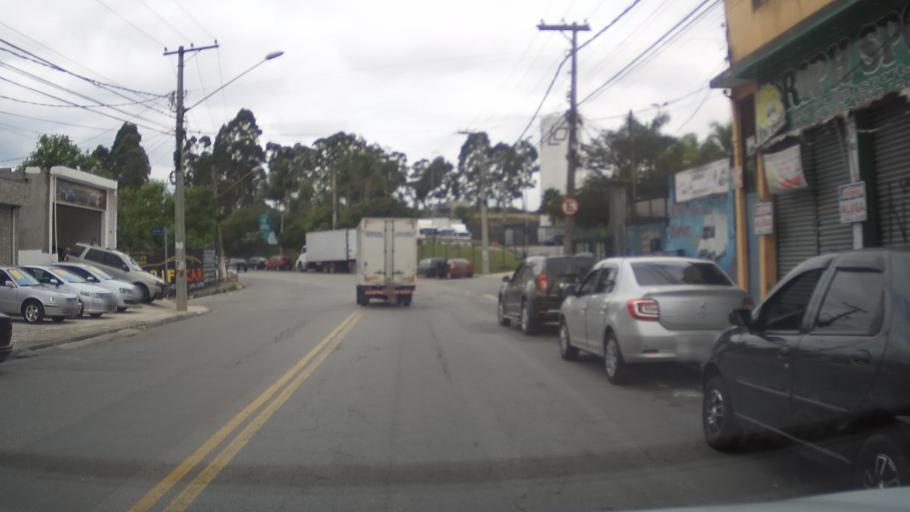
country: BR
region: Sao Paulo
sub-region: Itaquaquecetuba
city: Itaquaquecetuba
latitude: -23.4257
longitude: -46.4295
